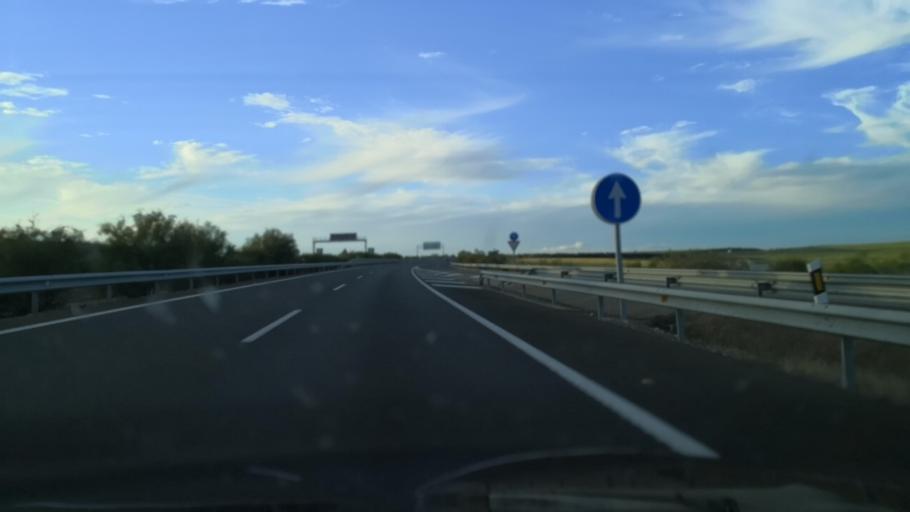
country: ES
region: Extremadura
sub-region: Provincia de Badajoz
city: Merida
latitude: 38.9522
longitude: -6.3432
